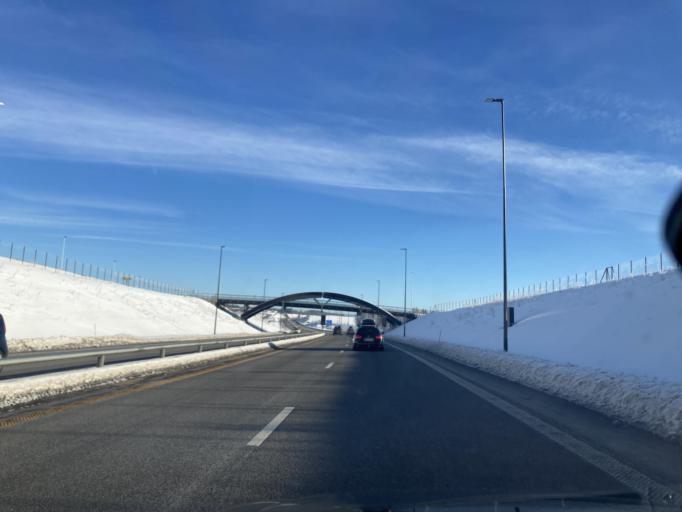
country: NO
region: Hedmark
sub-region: Loten
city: Loten
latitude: 60.8419
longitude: 11.3495
